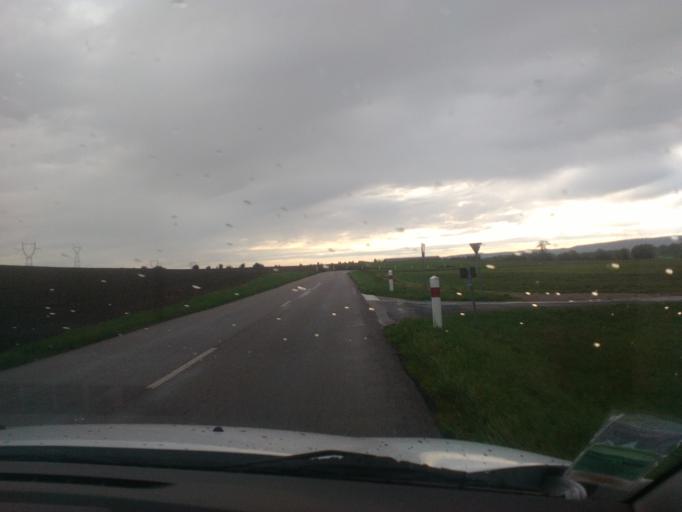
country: FR
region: Lorraine
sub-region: Departement des Vosges
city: Aydoilles
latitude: 48.2576
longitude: 6.5407
